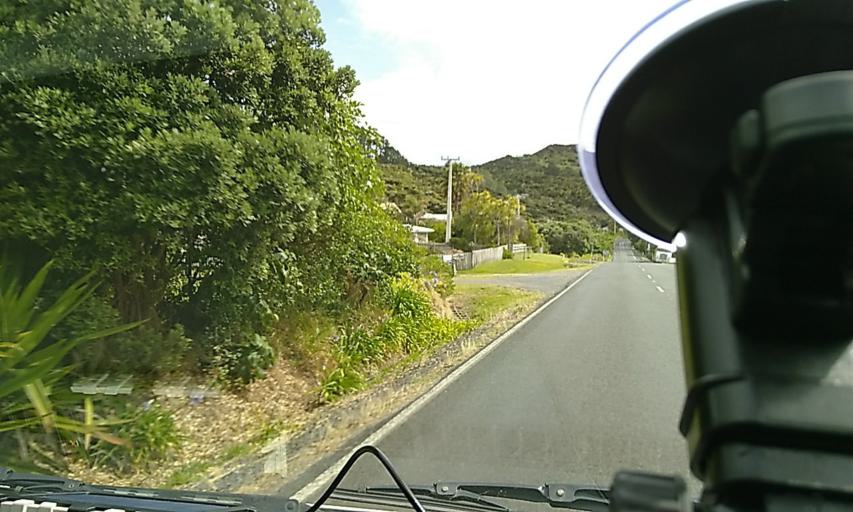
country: NZ
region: Northland
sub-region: Far North District
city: Ahipara
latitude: -35.5339
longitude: 173.3885
